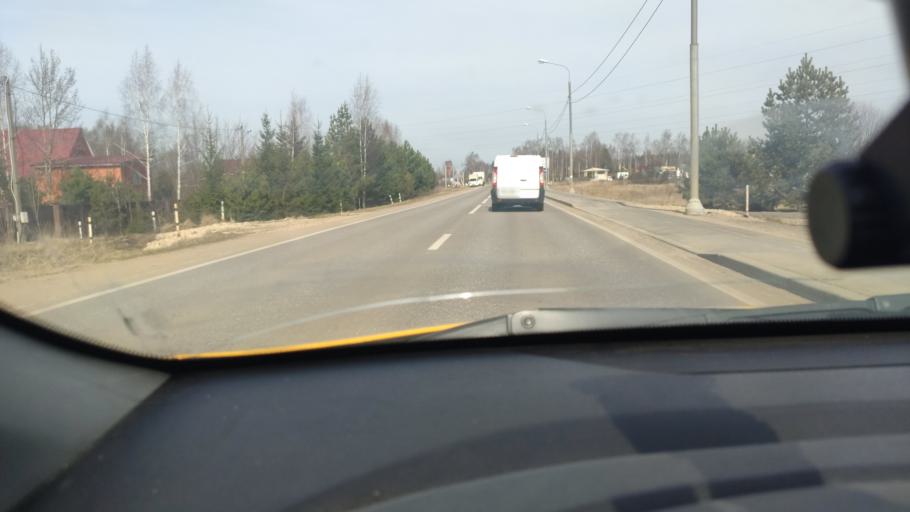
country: RU
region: Moskovskaya
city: Ruza
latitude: 55.7531
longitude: 36.1443
